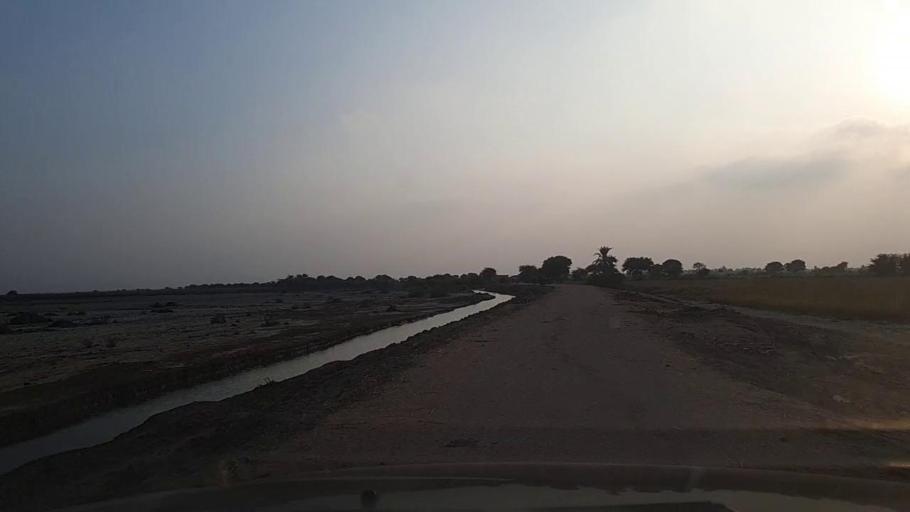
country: PK
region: Sindh
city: Jati
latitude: 24.5347
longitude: 68.3587
